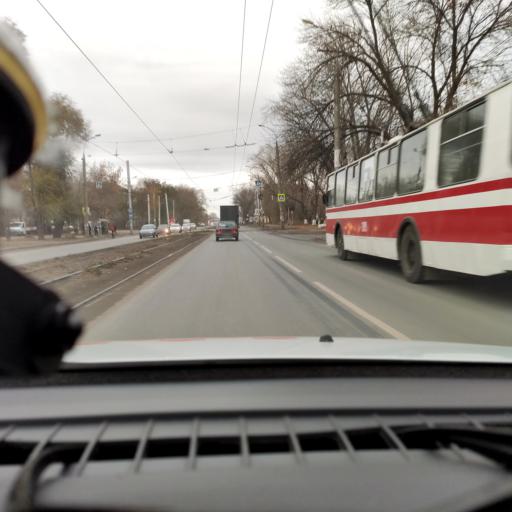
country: RU
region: Samara
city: Smyshlyayevka
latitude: 53.1965
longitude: 50.2895
